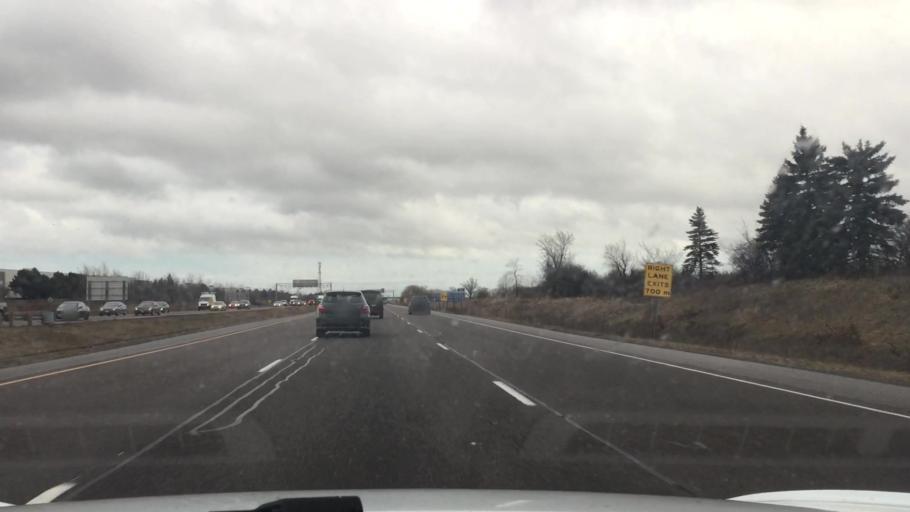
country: CA
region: Ontario
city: Oakville
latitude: 43.5195
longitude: -79.7088
